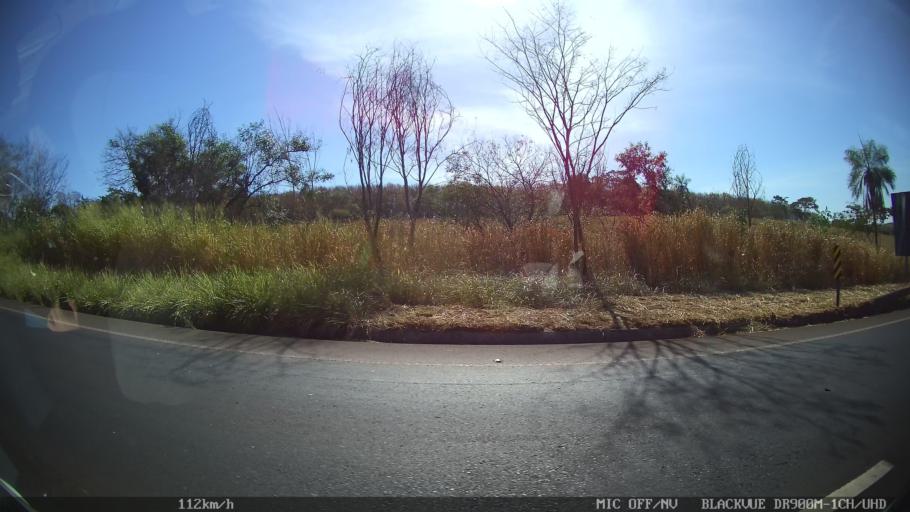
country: BR
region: Sao Paulo
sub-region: Olimpia
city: Olimpia
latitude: -20.6186
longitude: -48.7642
